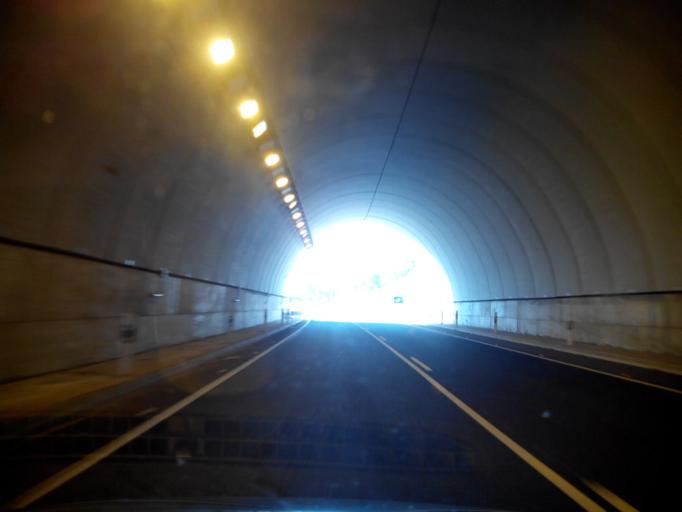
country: ES
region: Catalonia
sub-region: Provincia de Barcelona
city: Sant Joan de Vilatorrada
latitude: 41.7301
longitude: 1.7805
